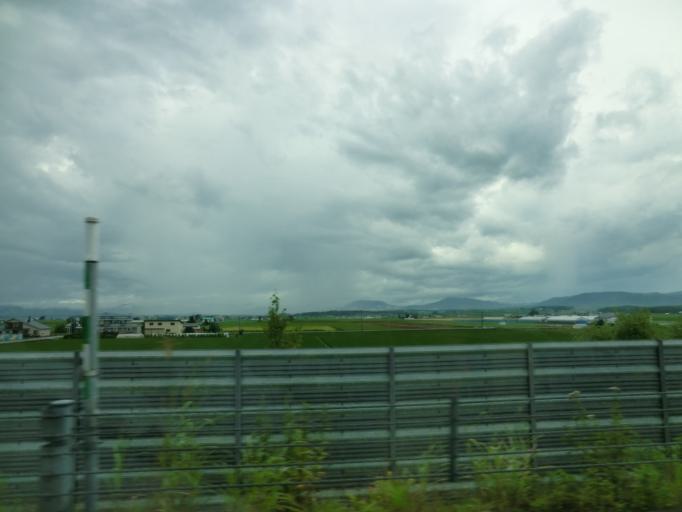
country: JP
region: Hokkaido
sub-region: Asahikawa-shi
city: Asahikawa
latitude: 43.8459
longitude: 142.4198
